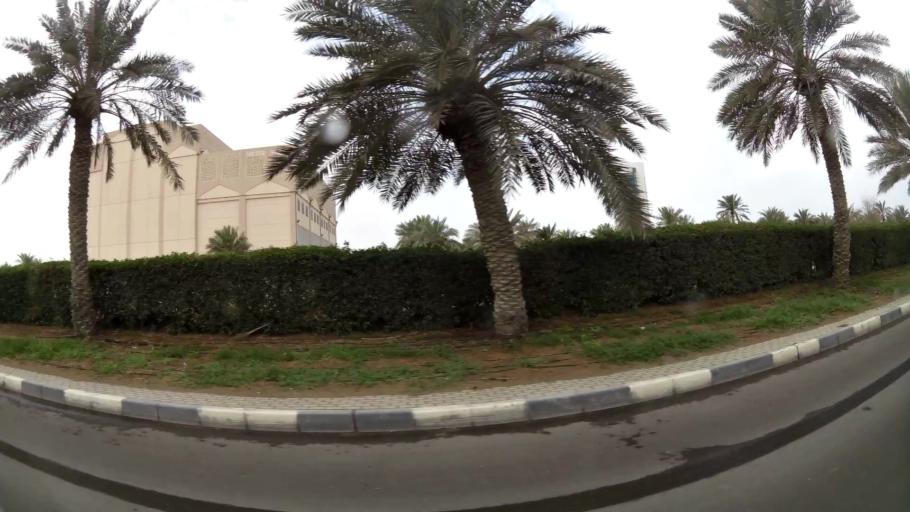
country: AE
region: Abu Dhabi
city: Abu Dhabi
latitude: 24.4602
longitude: 54.3998
